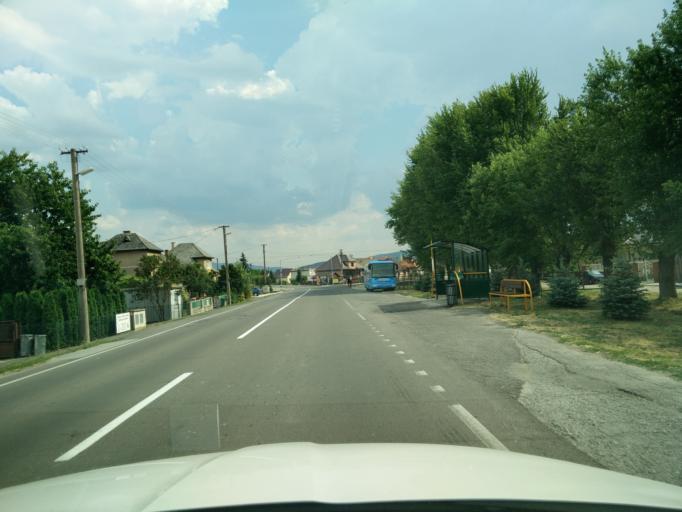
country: SK
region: Nitriansky
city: Novaky
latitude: 48.7506
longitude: 18.4972
